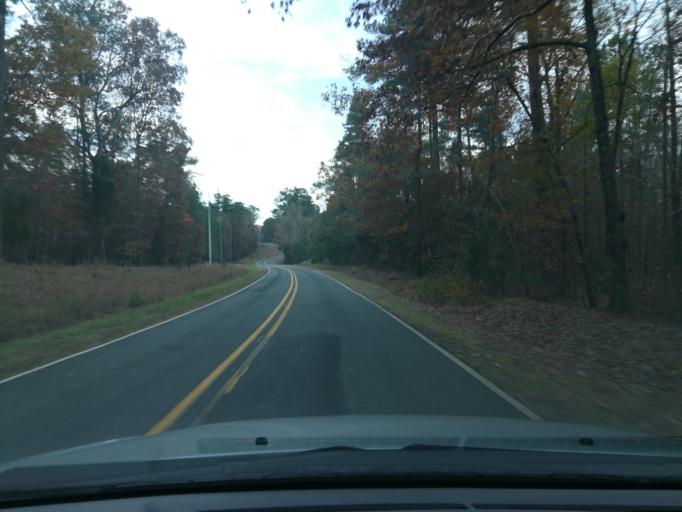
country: US
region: North Carolina
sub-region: Orange County
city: Hillsborough
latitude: 36.0096
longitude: -79.0455
